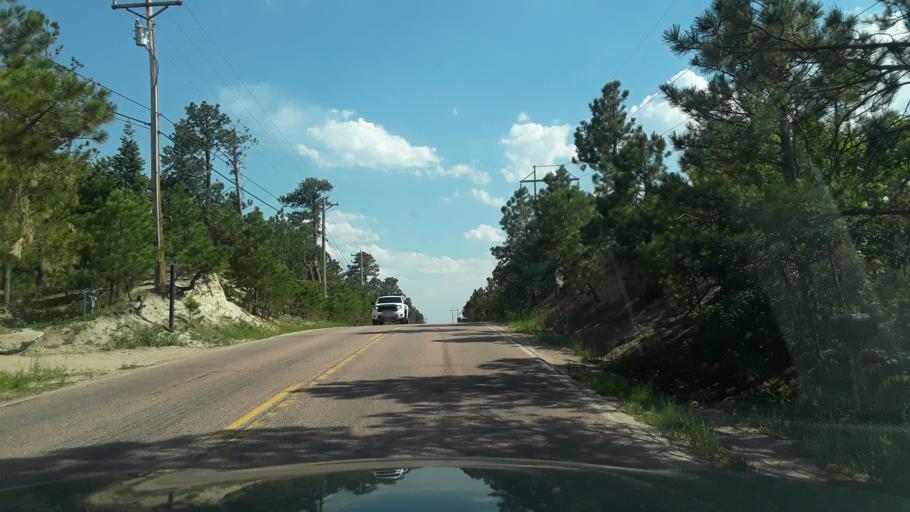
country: US
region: Colorado
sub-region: El Paso County
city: Gleneagle
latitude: 39.0445
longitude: -104.7849
